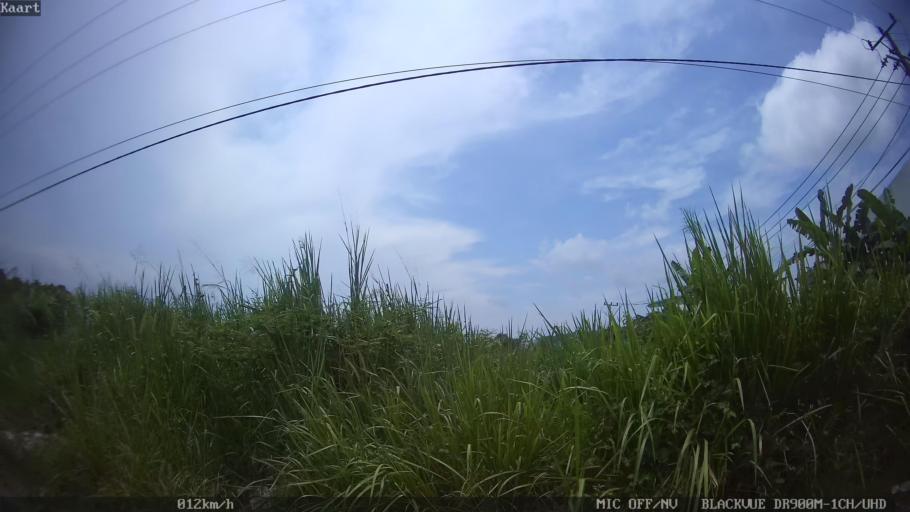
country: ID
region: Lampung
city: Bandarlampung
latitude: -5.4115
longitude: 105.1994
